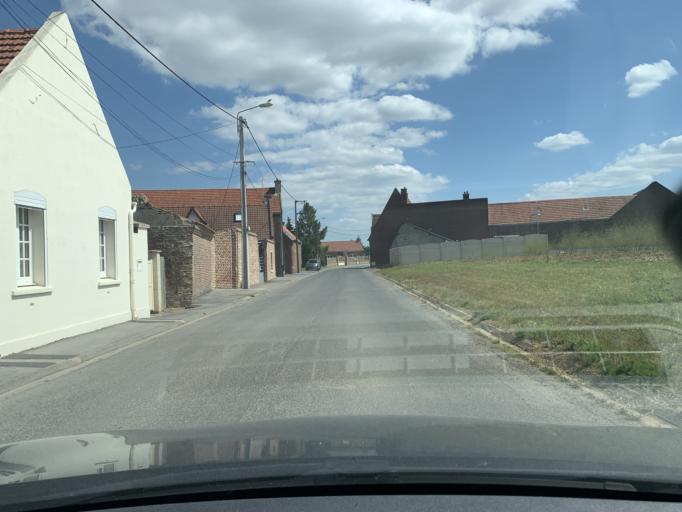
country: FR
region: Nord-Pas-de-Calais
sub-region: Departement du Nord
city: Aubigny-au-Bac
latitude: 50.2293
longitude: 3.1716
